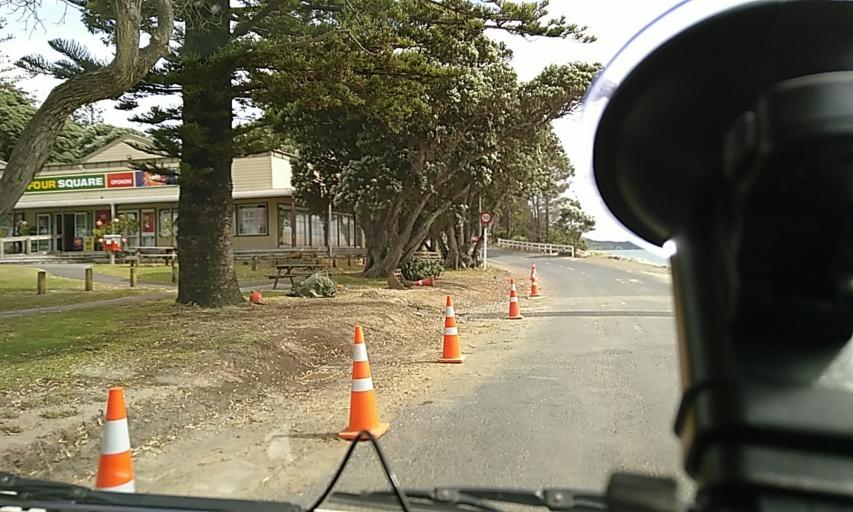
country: NZ
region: Northland
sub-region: Far North District
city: Ahipara
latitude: -35.5054
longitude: 173.3906
